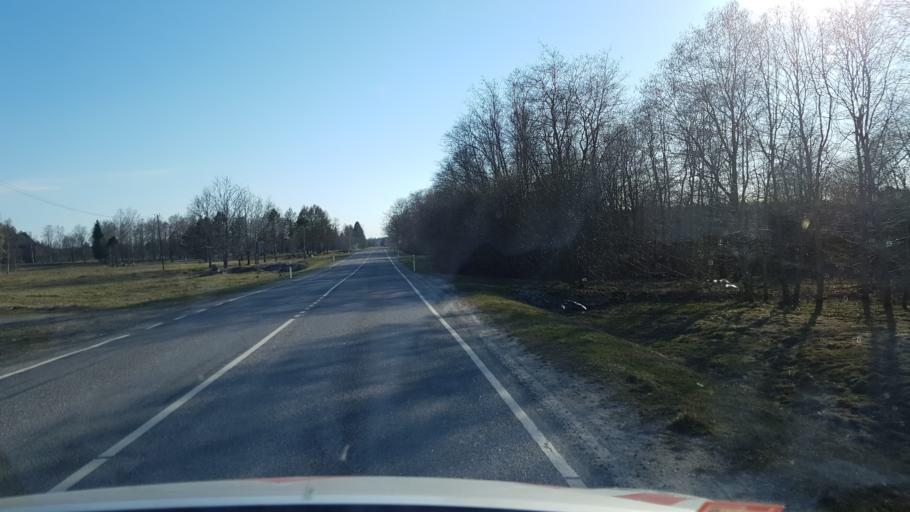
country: EE
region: Ida-Virumaa
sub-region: Kohtla-Jaerve linn
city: Kohtla-Jarve
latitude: 59.3295
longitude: 27.2724
